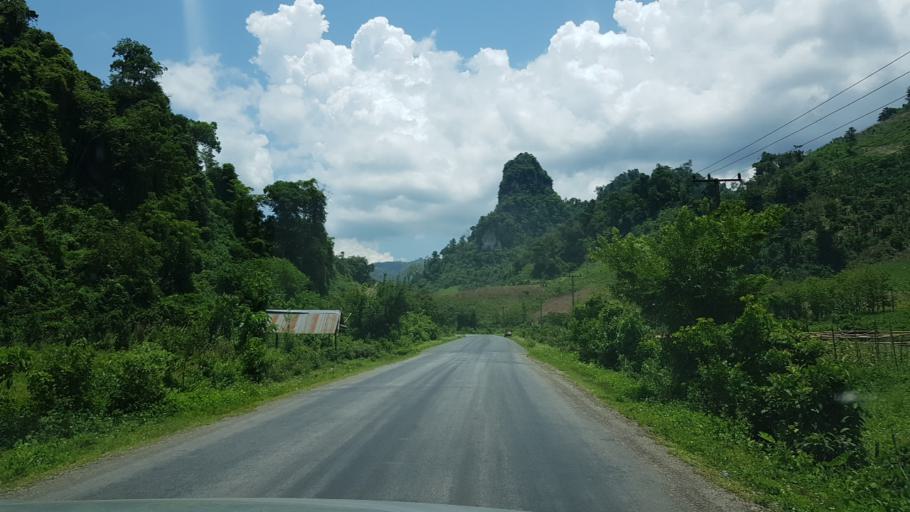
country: LA
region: Vientiane
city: Muang Kasi
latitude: 19.1236
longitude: 102.2572
